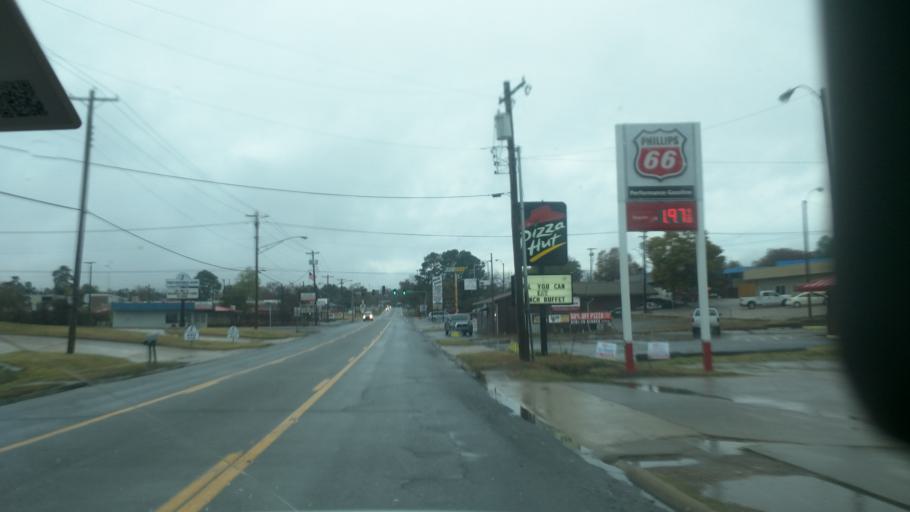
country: US
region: Arkansas
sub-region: Franklin County
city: Ozark
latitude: 35.4888
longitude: -93.8414
